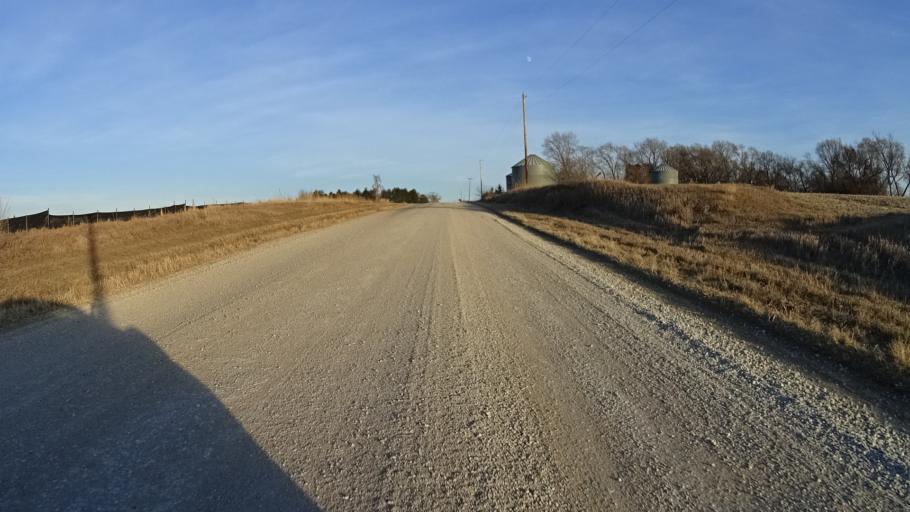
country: US
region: Nebraska
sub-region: Sarpy County
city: Springfield
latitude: 41.1326
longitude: -96.1087
